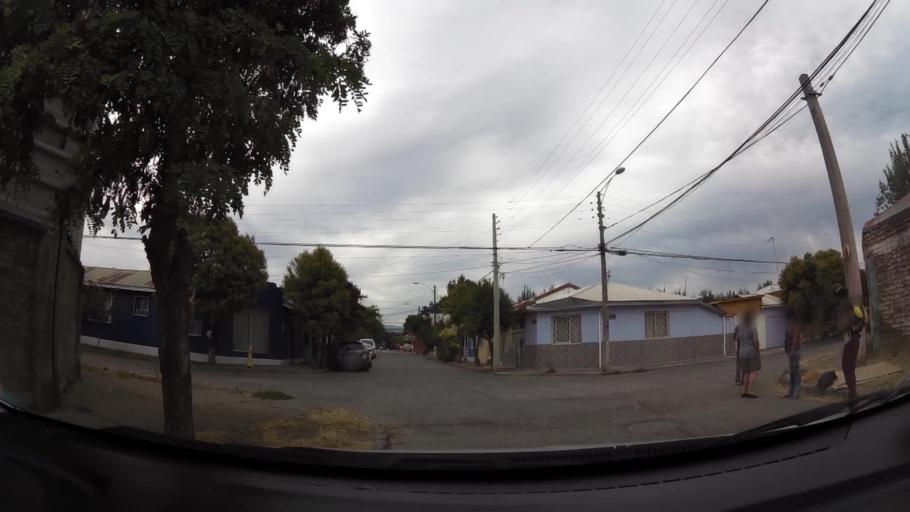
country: CL
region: O'Higgins
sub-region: Provincia de Cachapoal
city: Rancagua
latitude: -34.1593
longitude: -70.7454
